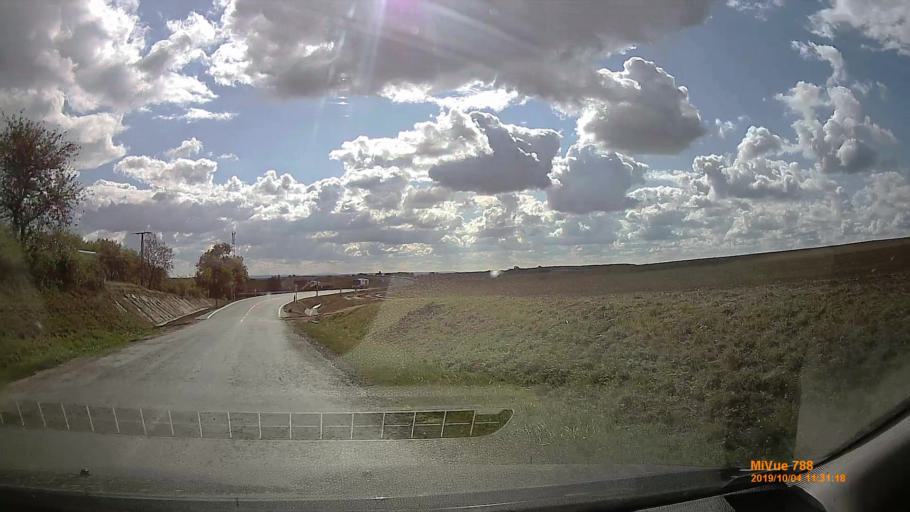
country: HU
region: Somogy
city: Kaposvar
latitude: 46.5166
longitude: 17.8076
